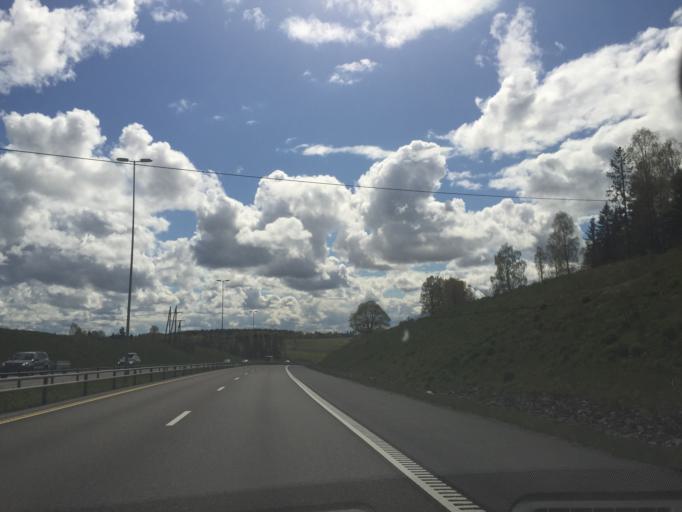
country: NO
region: Akershus
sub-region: Eidsvoll
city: Raholt
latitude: 60.2460
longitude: 11.1825
